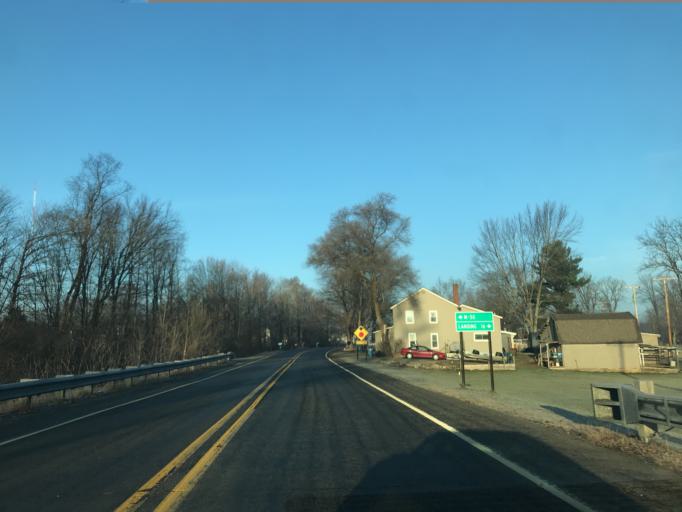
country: US
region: Michigan
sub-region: Eaton County
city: Eaton Rapids
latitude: 42.4421
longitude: -84.5579
